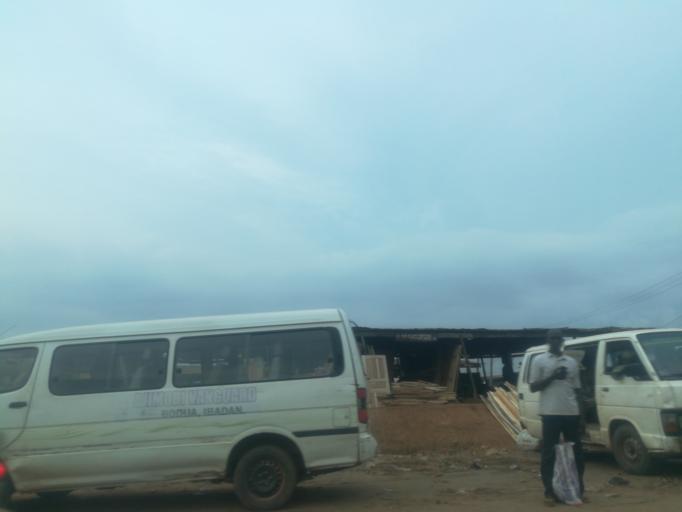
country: NG
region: Oyo
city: Ibadan
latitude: 7.4357
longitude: 3.9185
